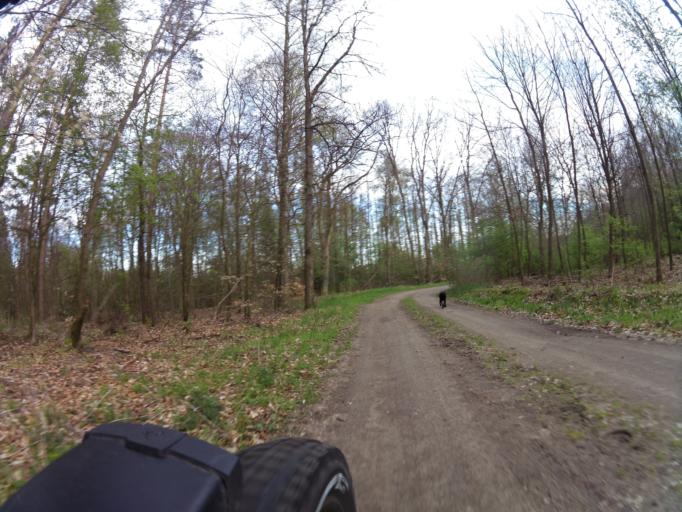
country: PL
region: West Pomeranian Voivodeship
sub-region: Powiat lobeski
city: Lobez
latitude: 53.7394
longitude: 15.6325
